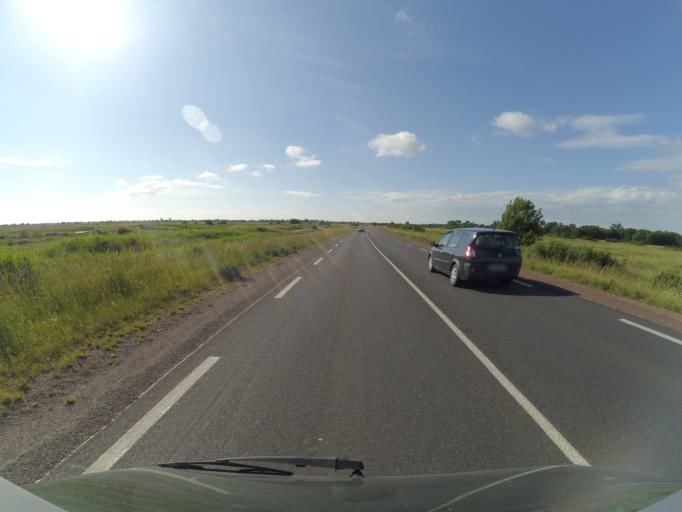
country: FR
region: Poitou-Charentes
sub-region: Departement de la Charente-Maritime
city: Saint-Agnant
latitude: 45.8565
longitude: -0.9643
